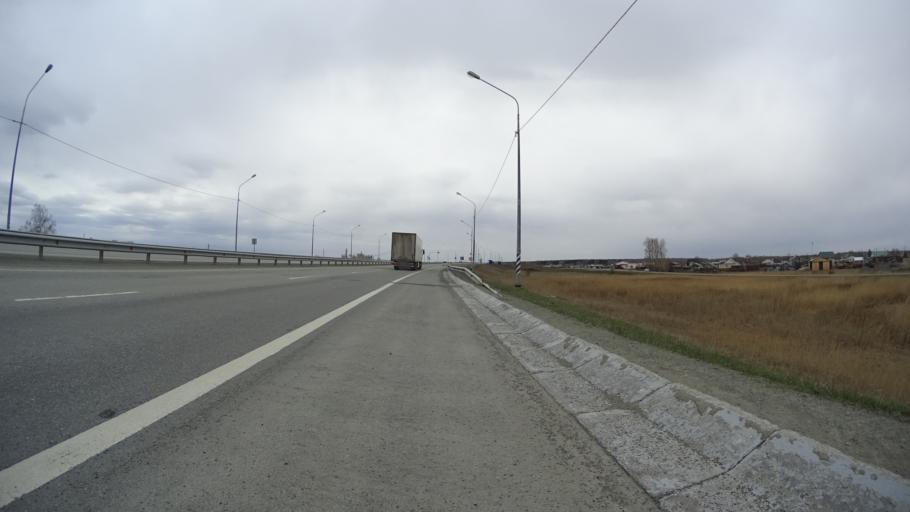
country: RU
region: Chelyabinsk
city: Yemanzhelinka
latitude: 54.7987
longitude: 61.3085
